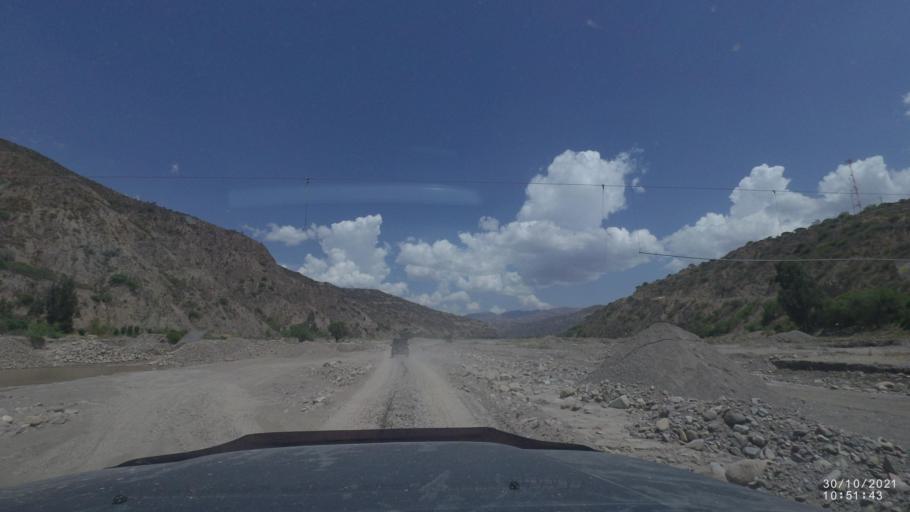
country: BO
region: Cochabamba
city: Sipe Sipe
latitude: -17.5537
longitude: -66.4752
